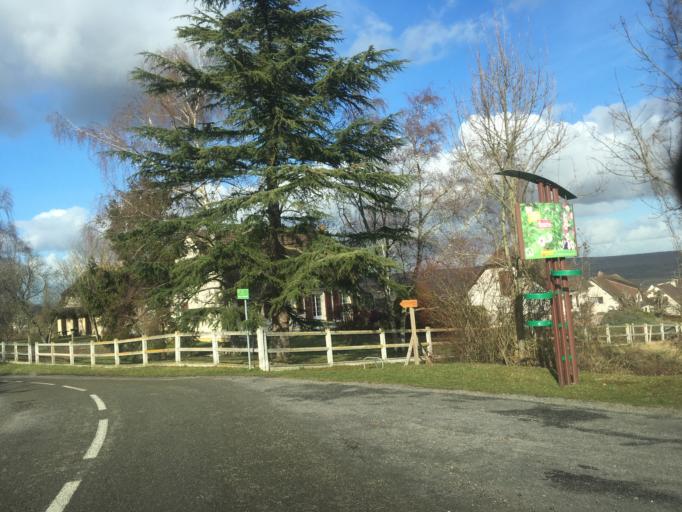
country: FR
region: Haute-Normandie
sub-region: Departement de l'Eure
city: Saint-Marcel
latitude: 49.0902
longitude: 1.4448
